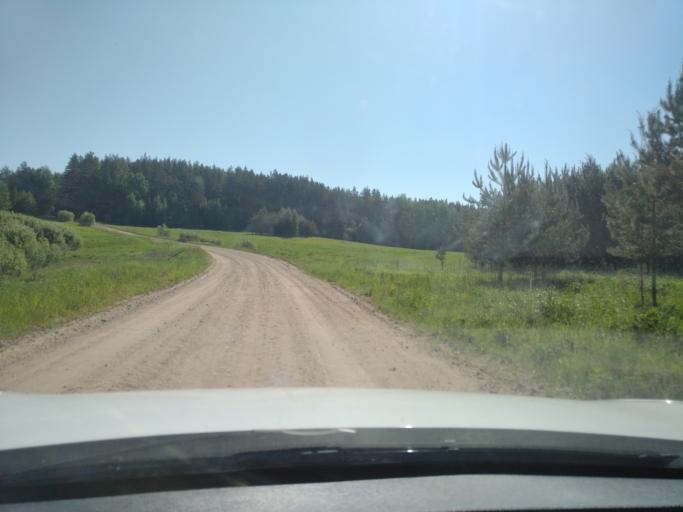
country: LT
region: Panevezys
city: Rokiskis
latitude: 55.7656
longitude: 25.6340
